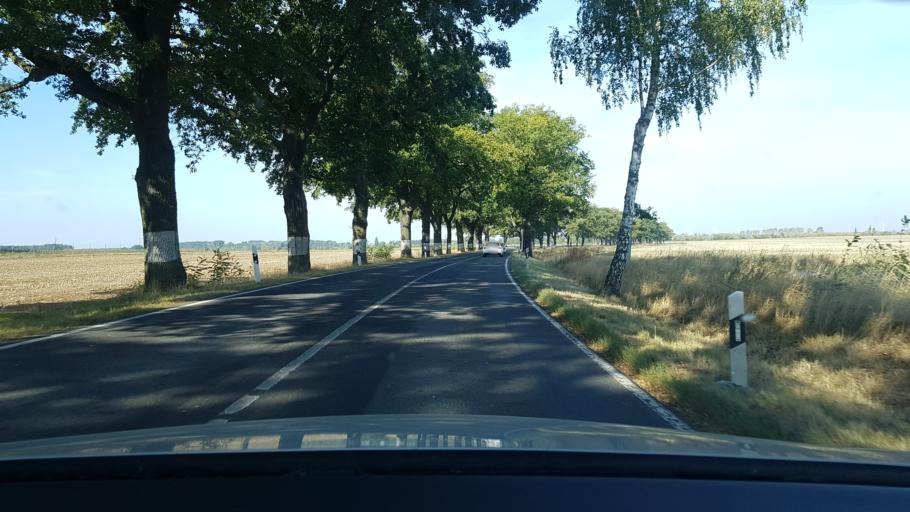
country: DE
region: Brandenburg
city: Beeskow
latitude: 52.1566
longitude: 14.3044
